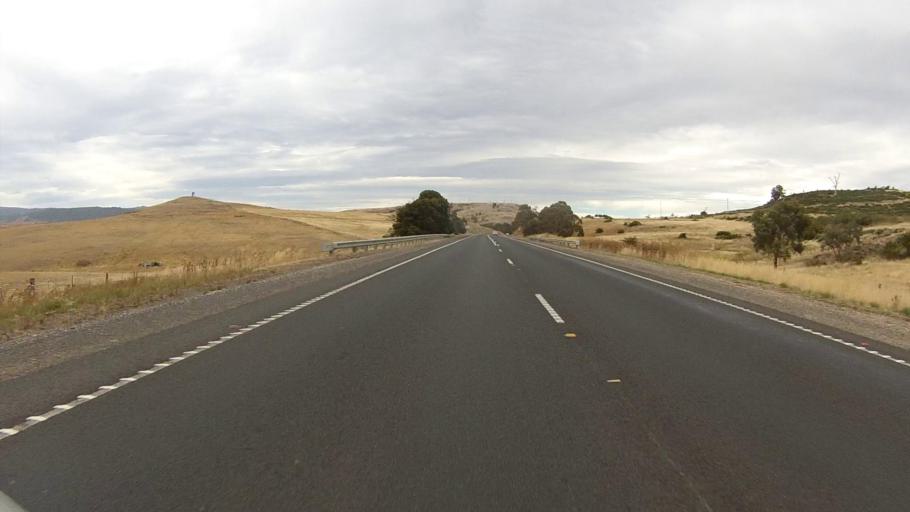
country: AU
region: Tasmania
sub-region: Brighton
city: Bridgewater
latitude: -42.3497
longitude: 147.3375
